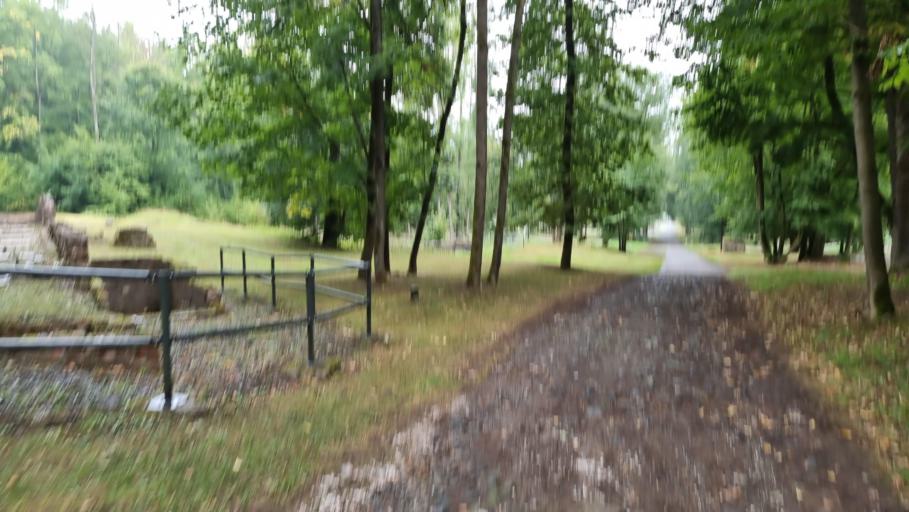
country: DE
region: Thuringia
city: Niedersachswerfen
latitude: 51.5357
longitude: 10.7436
